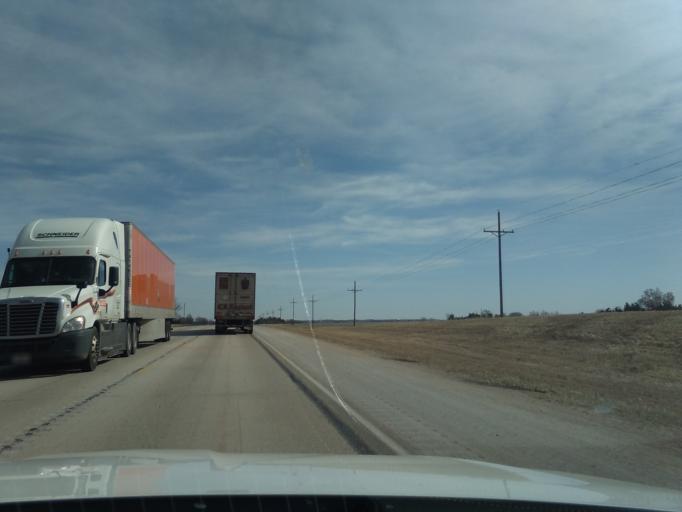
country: US
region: Nebraska
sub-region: Lancaster County
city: Hickman
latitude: 40.6540
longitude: -96.7230
